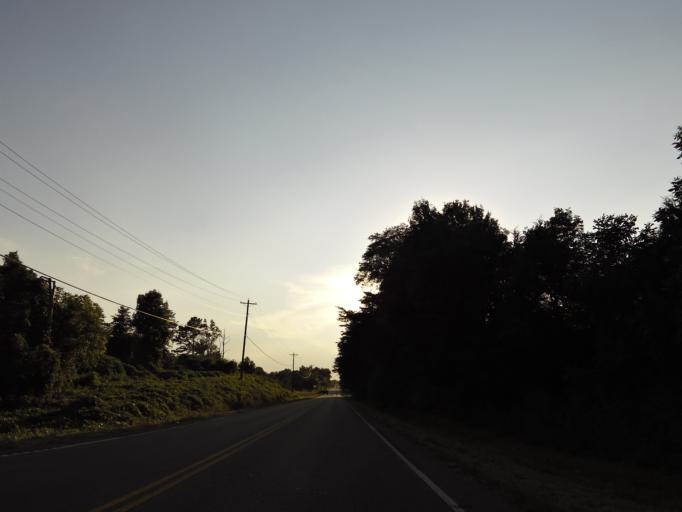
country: US
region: Tennessee
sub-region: McMinn County
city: Englewood
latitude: 35.4259
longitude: -84.5170
